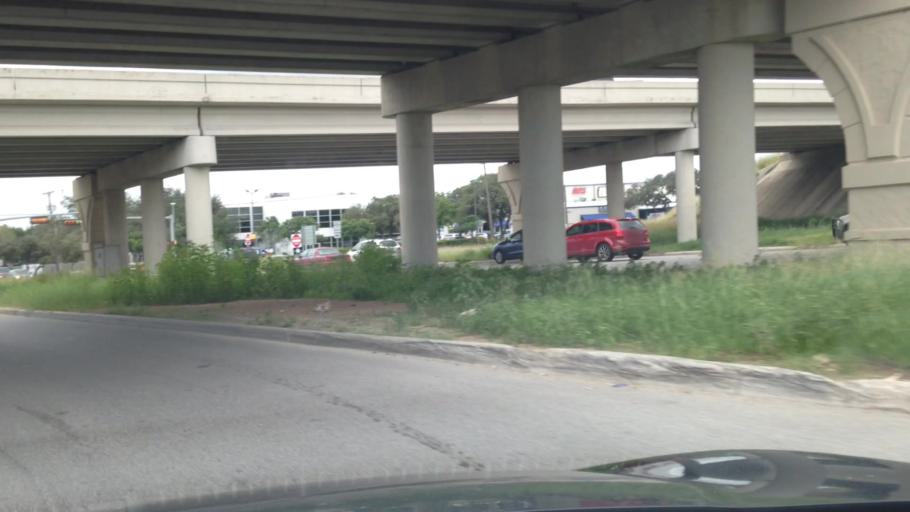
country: US
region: Texas
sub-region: Bexar County
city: Hollywood Park
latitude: 29.6091
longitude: -98.4924
